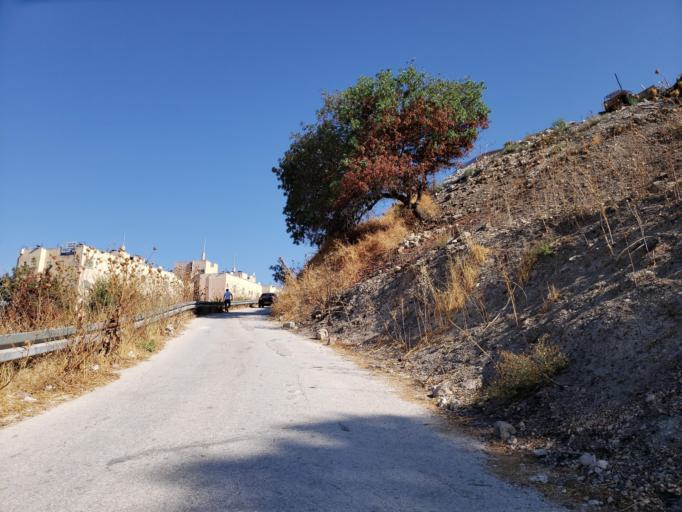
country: IL
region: Northern District
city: Safed
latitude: 32.9657
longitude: 35.4907
